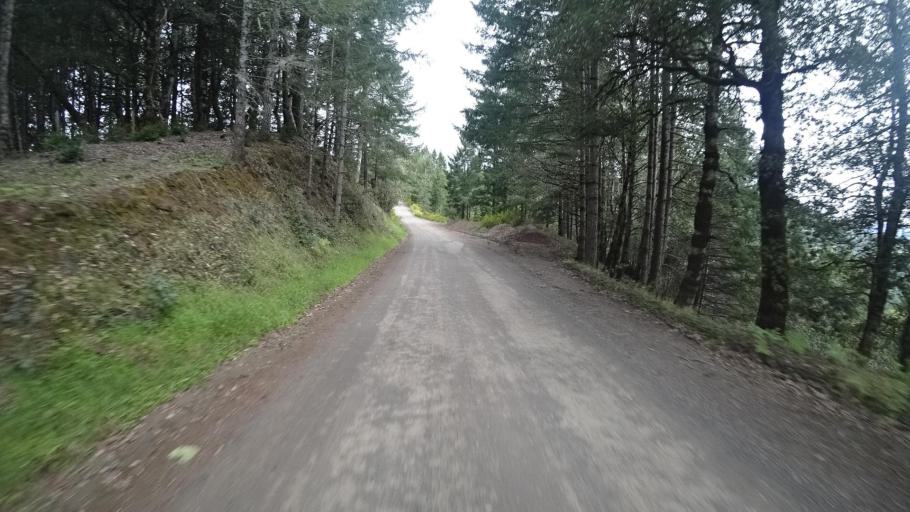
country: US
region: California
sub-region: Humboldt County
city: Redway
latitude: 40.2408
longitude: -123.7631
